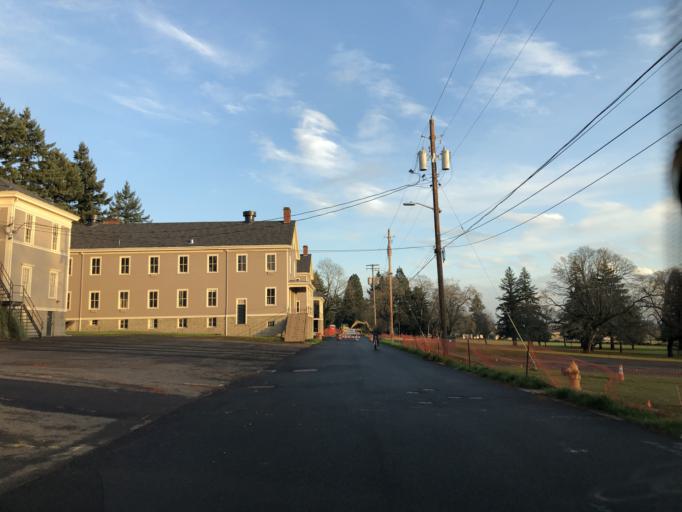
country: US
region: Washington
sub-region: Clark County
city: Vancouver
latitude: 45.6268
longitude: -122.6629
